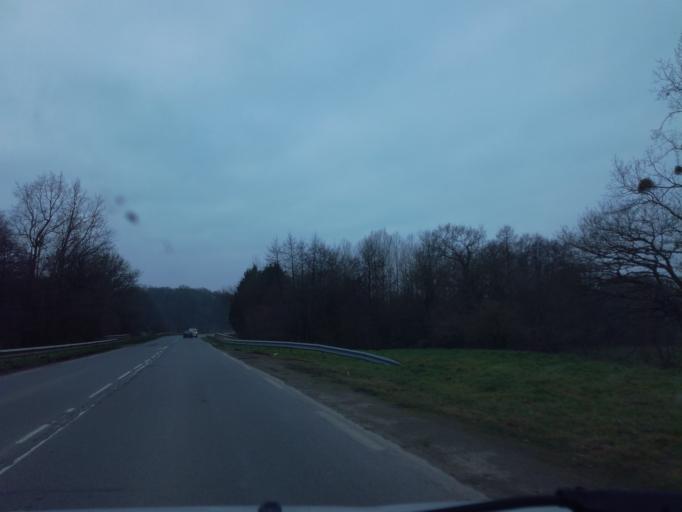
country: FR
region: Brittany
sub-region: Departement d'Ille-et-Vilaine
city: Gosne
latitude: 48.2383
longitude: -1.4636
